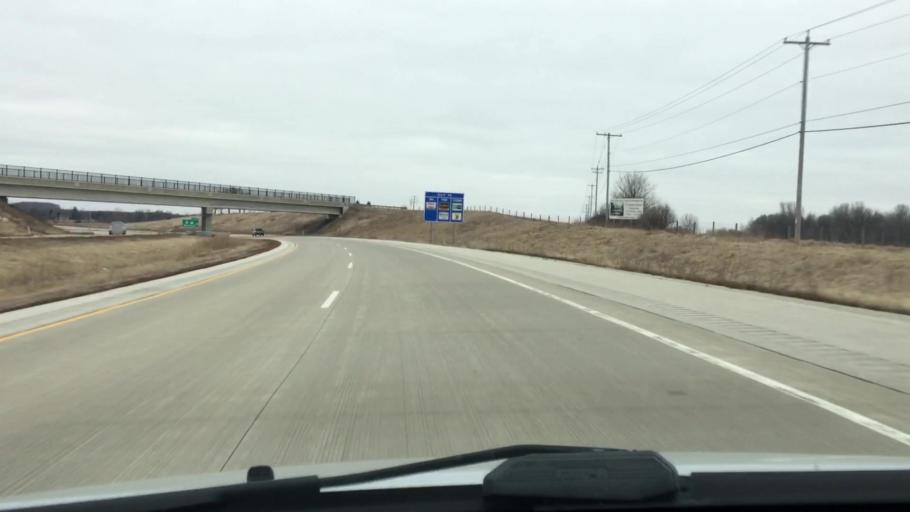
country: US
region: Wisconsin
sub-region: Jefferson County
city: Watertown
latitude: 43.1496
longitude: -88.7347
